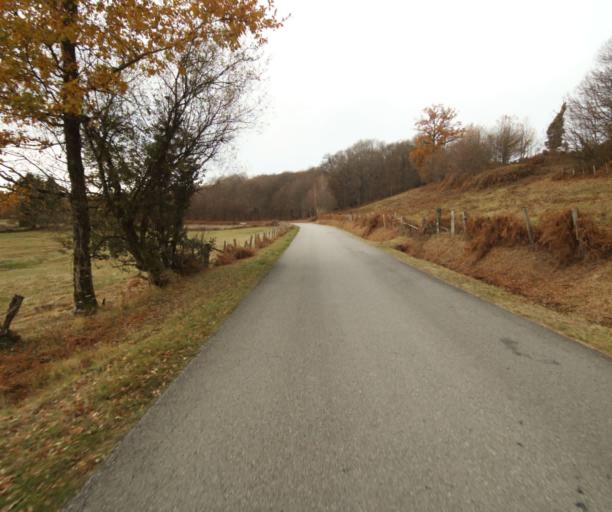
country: FR
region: Limousin
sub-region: Departement de la Correze
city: Sainte-Fortunade
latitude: 45.1815
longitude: 1.7545
